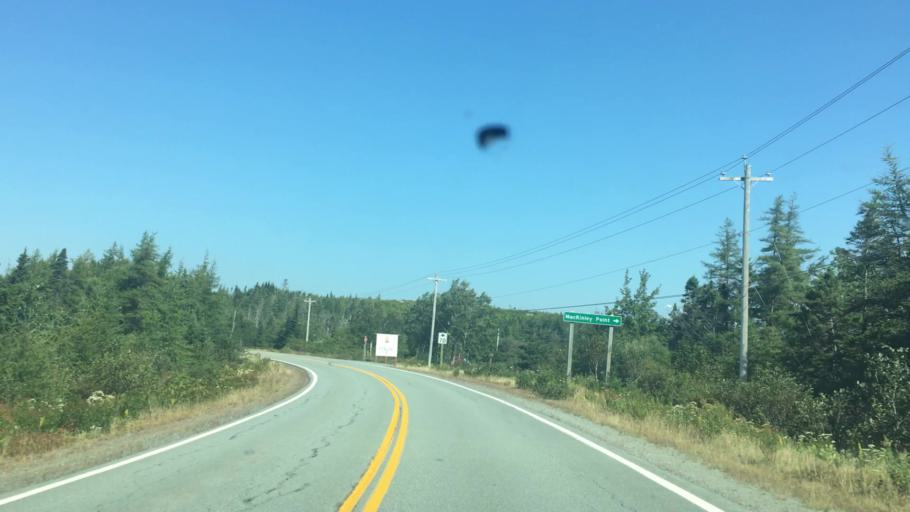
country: CA
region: Nova Scotia
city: Antigonish
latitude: 45.0209
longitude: -62.0314
